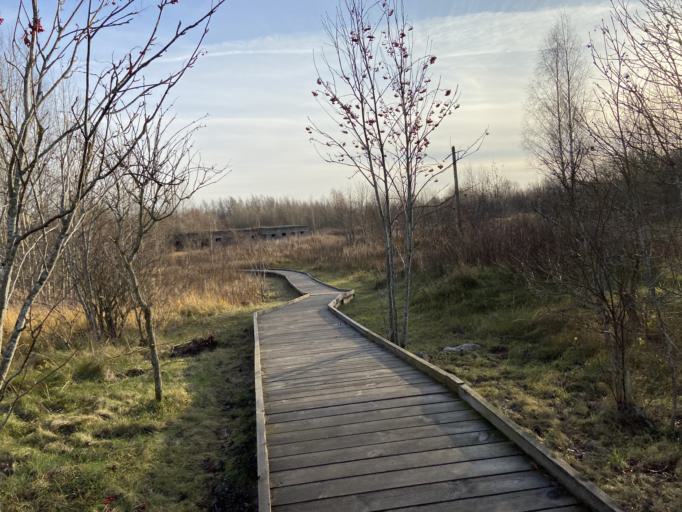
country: EE
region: Harju
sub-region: Tallinna linn
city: Tallinn
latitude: 59.4764
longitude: 24.7143
